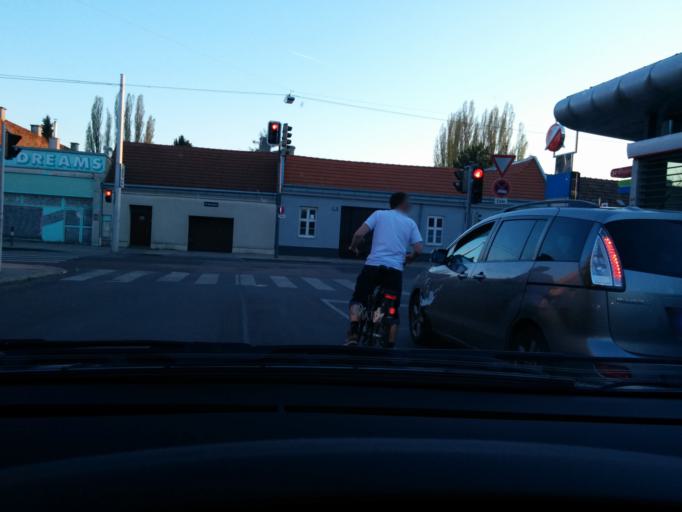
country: AT
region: Lower Austria
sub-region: Politischer Bezirk Modling
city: Vosendorf
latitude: 48.1279
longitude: 16.3097
